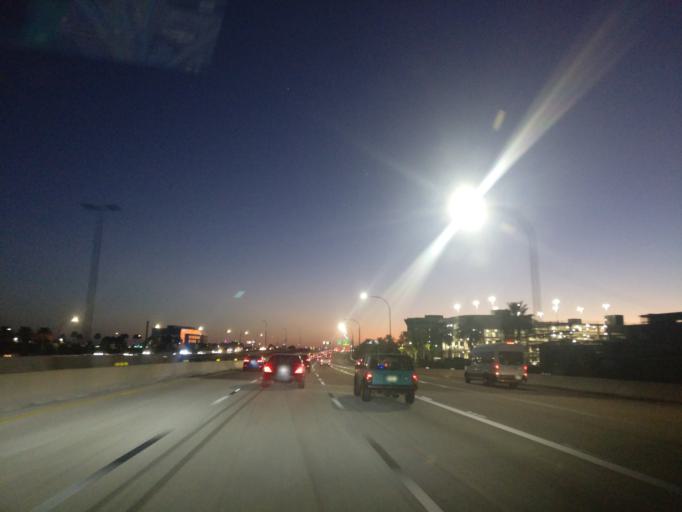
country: US
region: Florida
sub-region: Orange County
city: Oak Ridge
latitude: 28.4900
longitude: -81.4374
